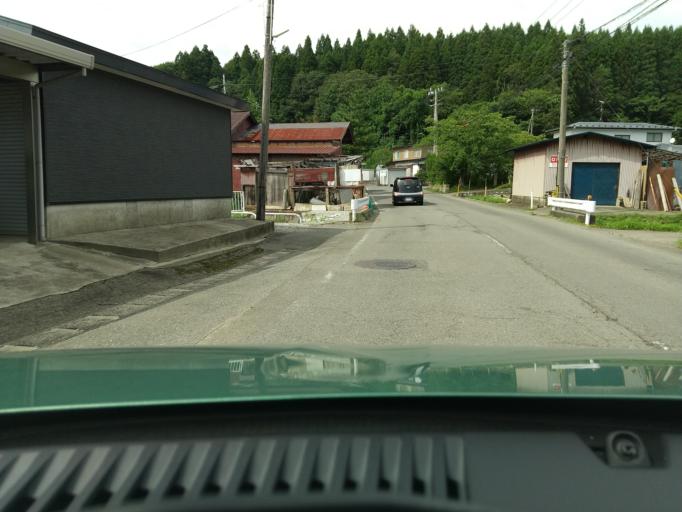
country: JP
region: Akita
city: Akita
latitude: 39.7799
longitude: 140.1349
